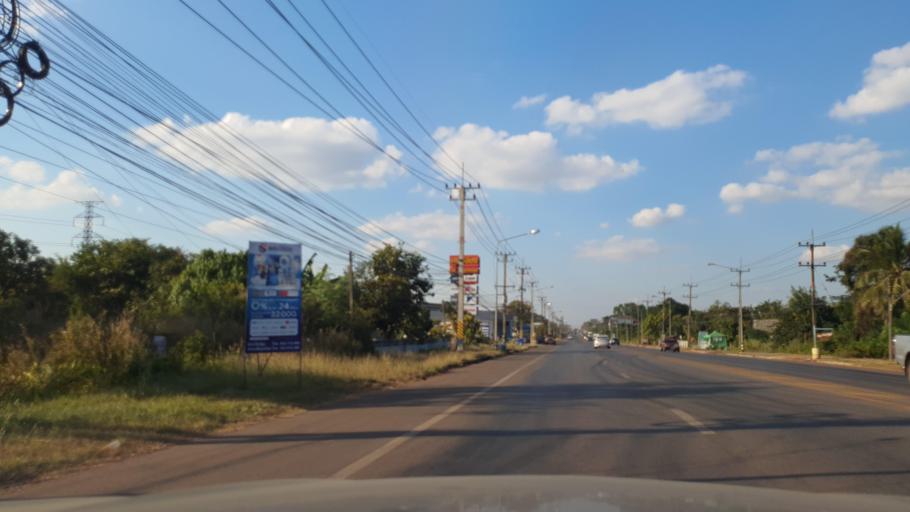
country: TH
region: Sakon Nakhon
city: Sakon Nakhon
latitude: 17.1689
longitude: 104.0999
